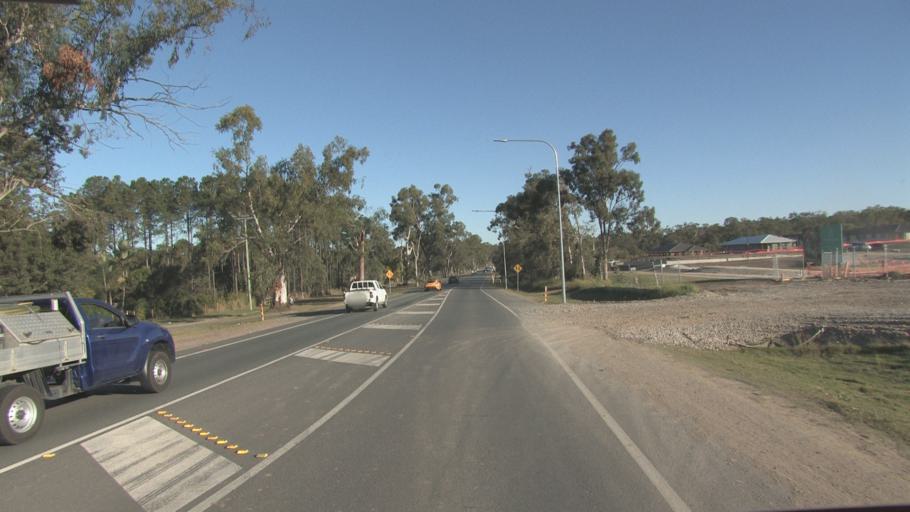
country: AU
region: Queensland
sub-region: Logan
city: Logan Reserve
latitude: -27.7119
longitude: 153.0933
